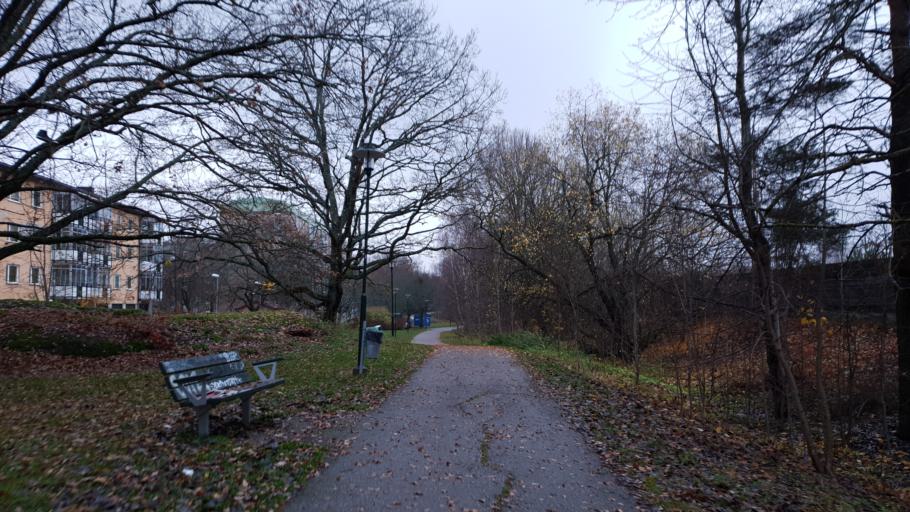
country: SE
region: Stockholm
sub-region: Stockholms Kommun
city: Arsta
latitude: 59.2419
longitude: 18.0831
